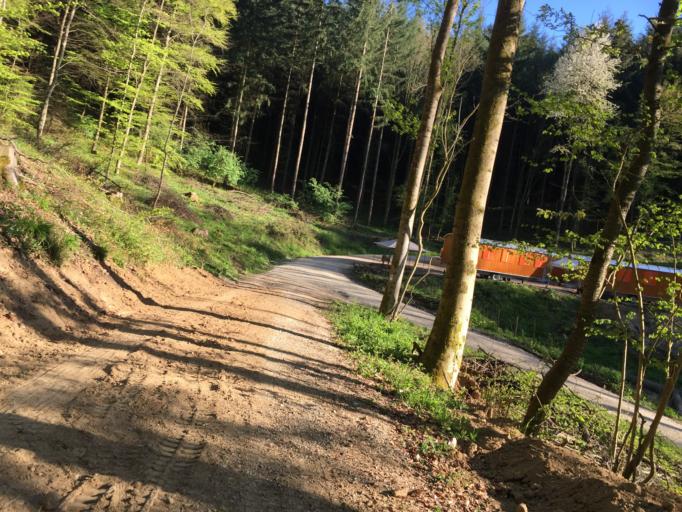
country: DE
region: Baden-Wuerttemberg
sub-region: Karlsruhe Region
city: Weinheim
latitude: 49.5143
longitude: 8.6791
